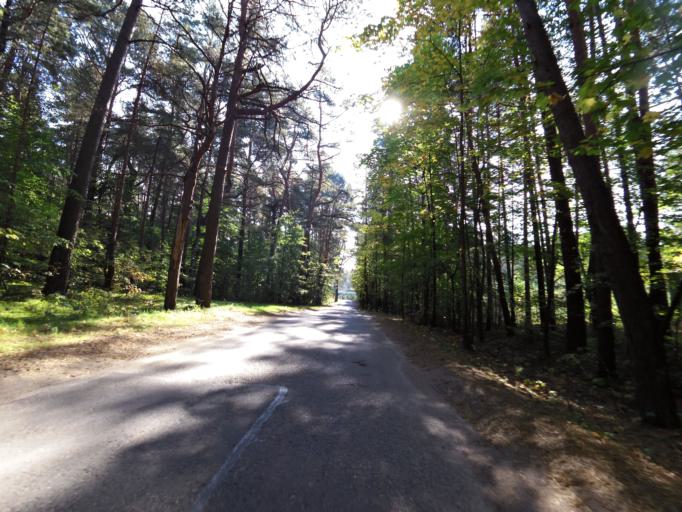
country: LT
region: Vilnius County
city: Rasos
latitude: 54.7318
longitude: 25.3119
